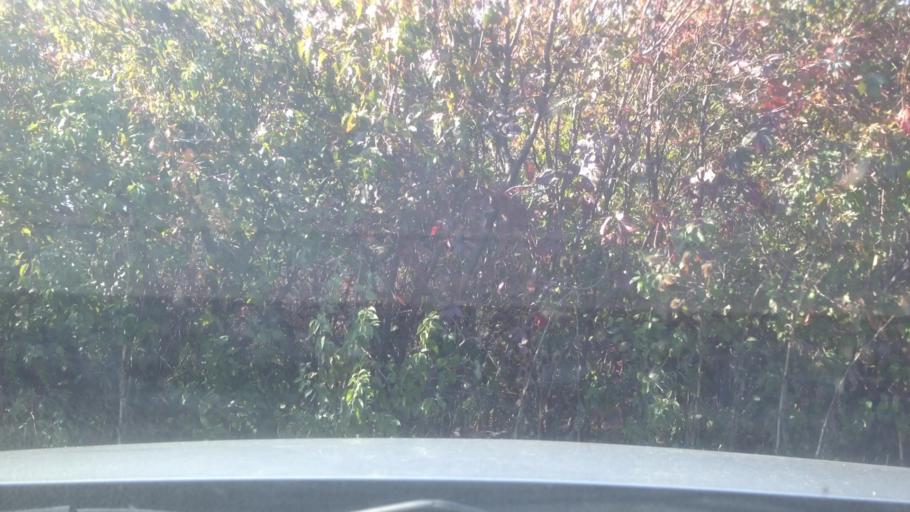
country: US
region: Illinois
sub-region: Will County
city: Monee
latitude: 41.4245
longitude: -87.7586
